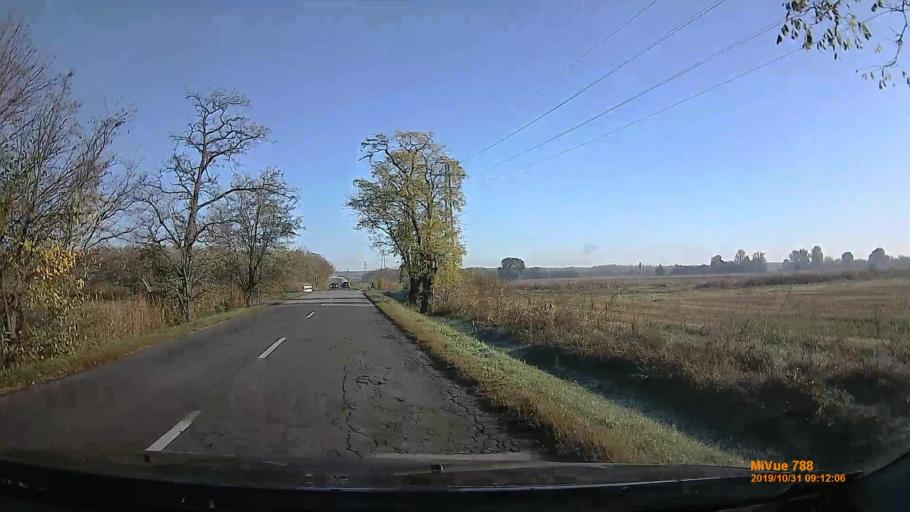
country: HU
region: Pest
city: Peteri
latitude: 47.3713
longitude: 19.3917
